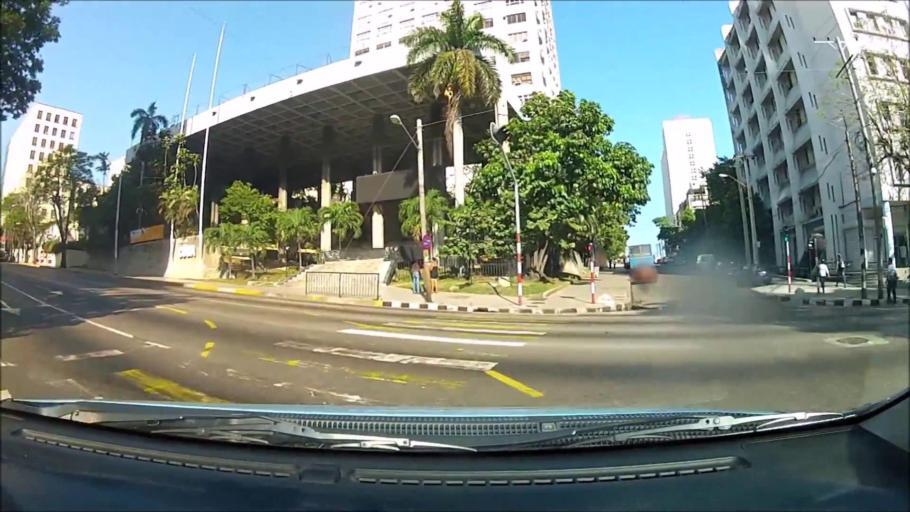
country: CU
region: La Habana
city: Havana
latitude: 23.1409
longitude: -82.3816
